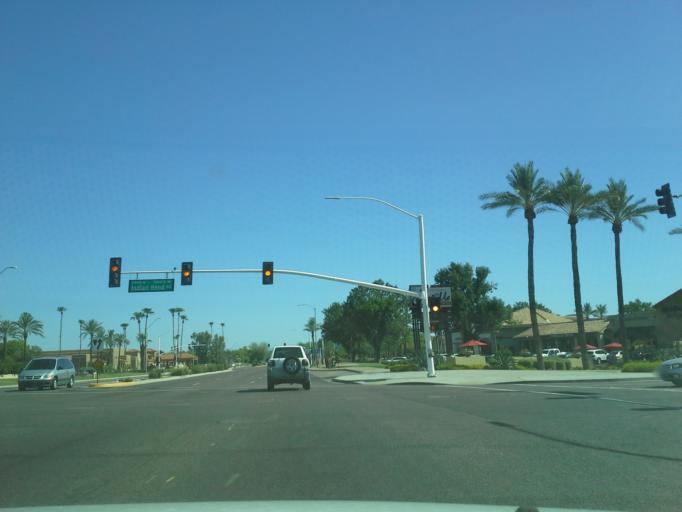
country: US
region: Arizona
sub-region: Maricopa County
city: Paradise Valley
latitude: 33.5384
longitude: -111.9256
